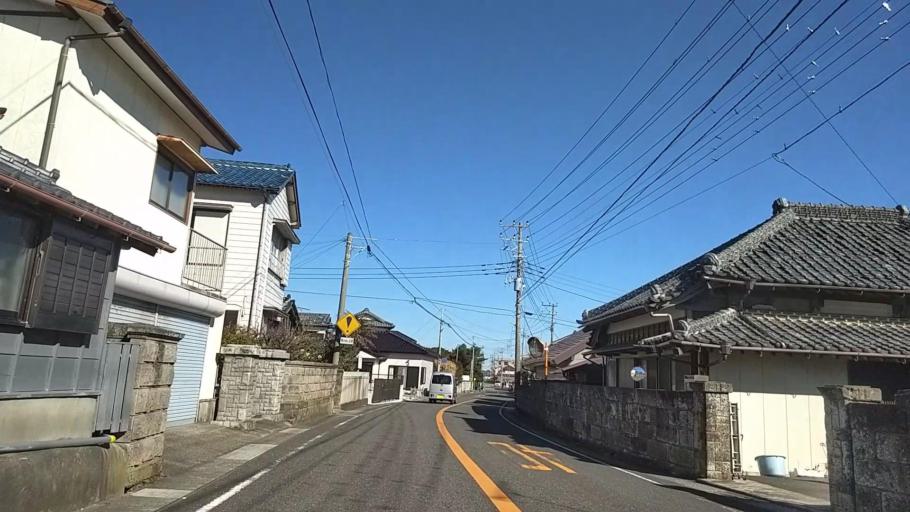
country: JP
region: Chiba
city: Tateyama
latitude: 34.9299
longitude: 139.9453
